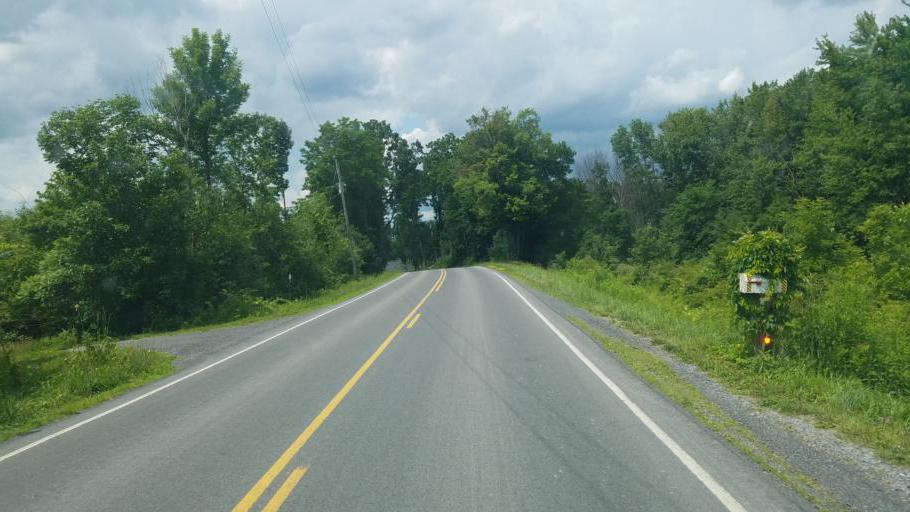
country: US
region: New York
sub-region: Seneca County
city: Waterloo
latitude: 42.9928
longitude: -76.8702
